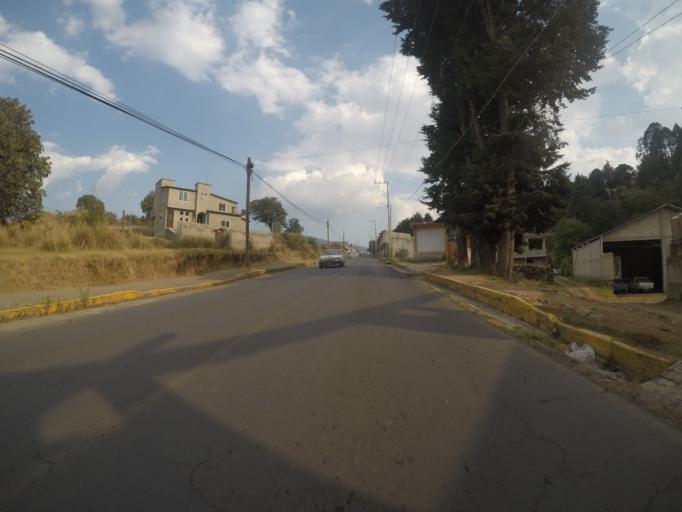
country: MX
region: Mexico
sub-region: Xalatlaco
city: El Aguila (La Mesa)
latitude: 19.1691
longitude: -99.4098
